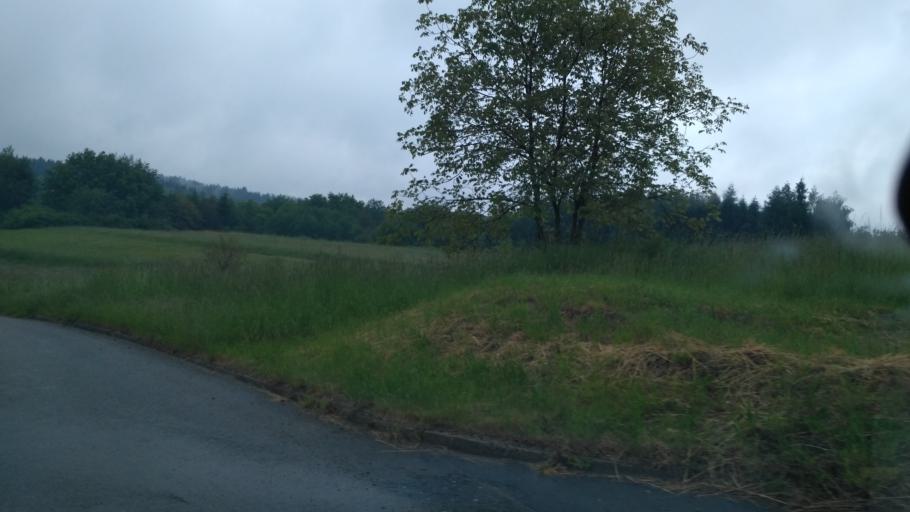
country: PL
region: Subcarpathian Voivodeship
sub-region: Powiat jasielski
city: Jaslo
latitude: 49.7649
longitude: 21.4872
